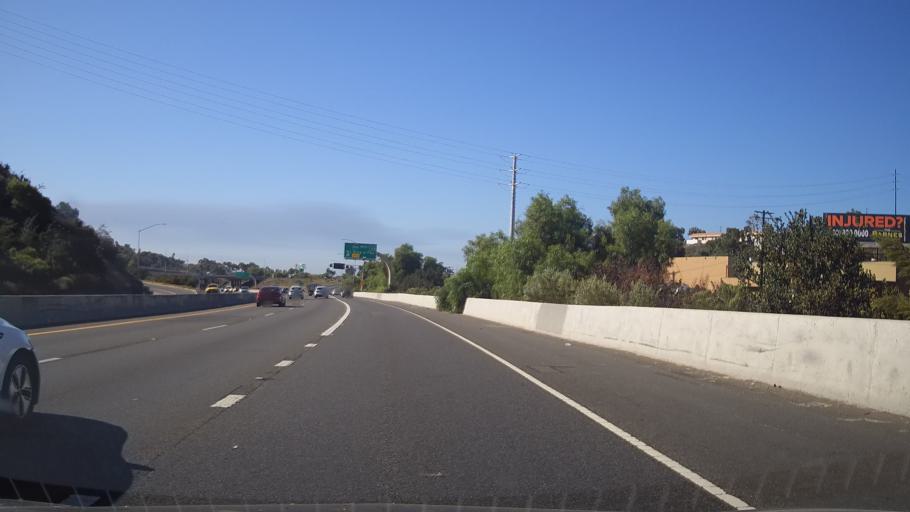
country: US
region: California
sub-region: San Diego County
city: San Diego
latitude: 32.7209
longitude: -117.1186
